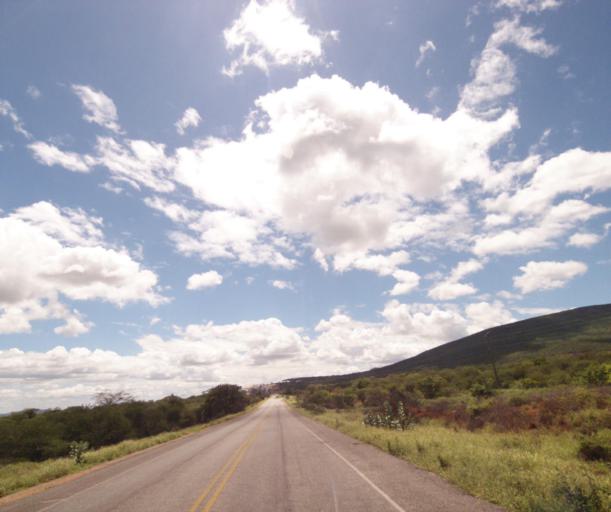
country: BR
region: Bahia
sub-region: Brumado
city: Brumado
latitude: -14.2371
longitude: -41.7110
